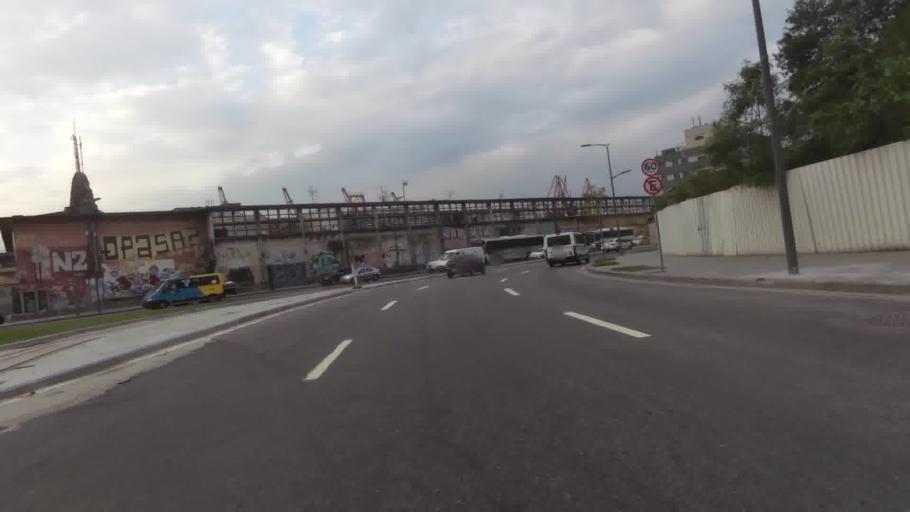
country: BR
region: Rio de Janeiro
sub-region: Rio De Janeiro
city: Rio de Janeiro
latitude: -22.8961
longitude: -43.2012
